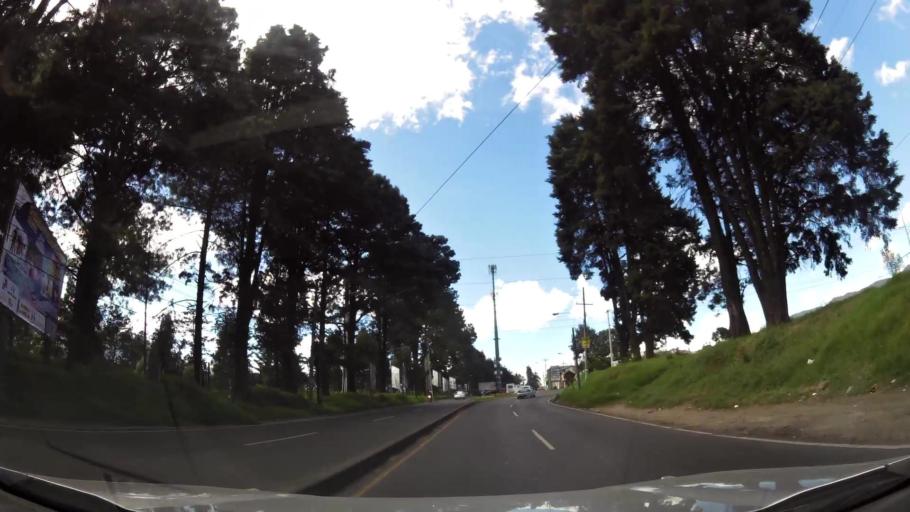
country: GT
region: Quetzaltenango
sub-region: Municipio de La Esperanza
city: La Esperanza
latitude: 14.8592
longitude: -91.5456
